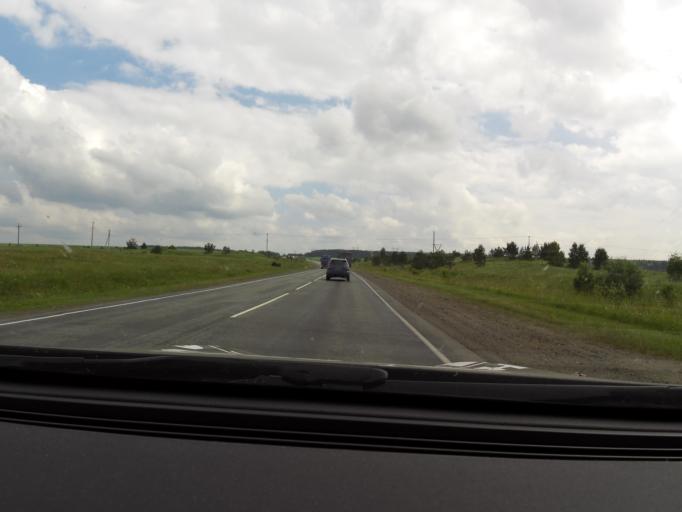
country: RU
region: Sverdlovsk
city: Achit
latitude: 56.8869
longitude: 57.6144
